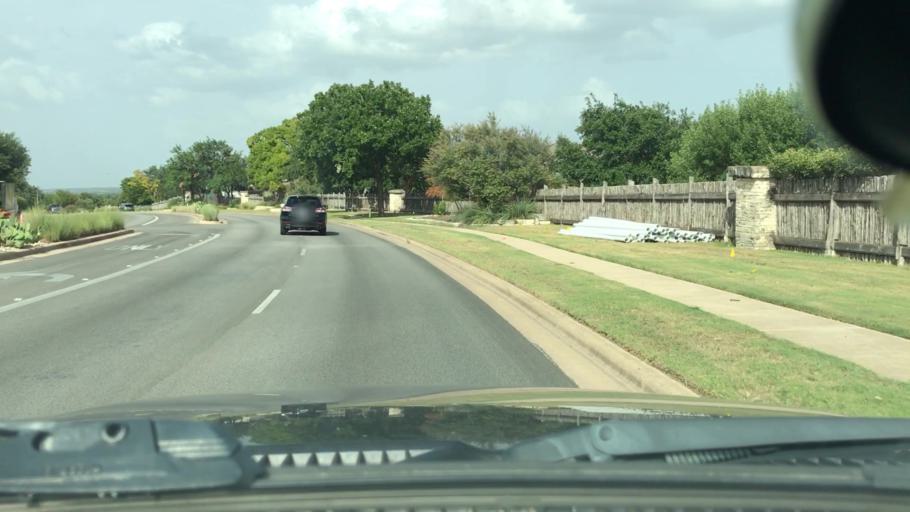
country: US
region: Texas
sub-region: Williamson County
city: Leander
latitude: 30.5468
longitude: -97.8594
